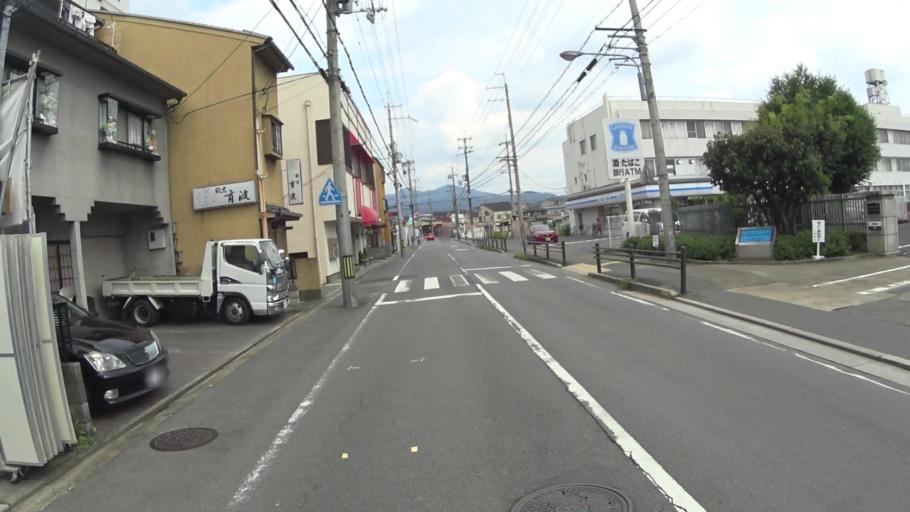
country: JP
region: Kyoto
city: Muko
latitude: 35.0072
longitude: 135.7065
